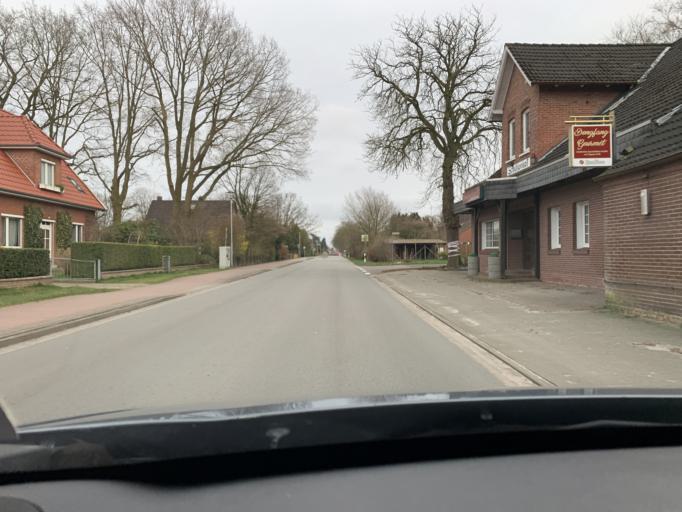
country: DE
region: Lower Saxony
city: Apen
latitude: 53.2270
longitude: 7.7477
